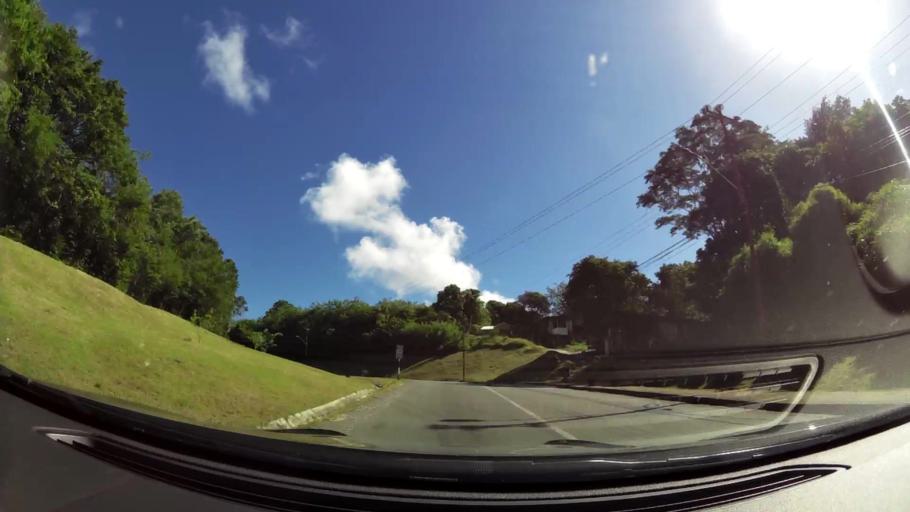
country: TT
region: Tobago
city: Scarborough
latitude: 11.1834
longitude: -60.7323
